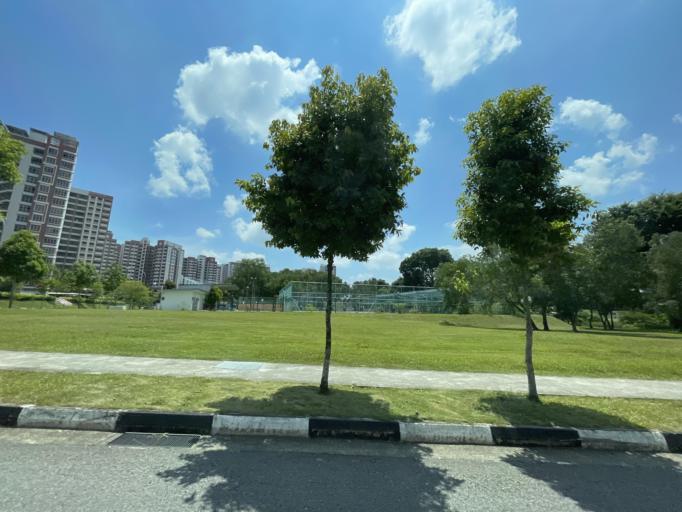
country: MY
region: Johor
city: Kampung Pasir Gudang Baru
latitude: 1.3829
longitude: 103.8796
